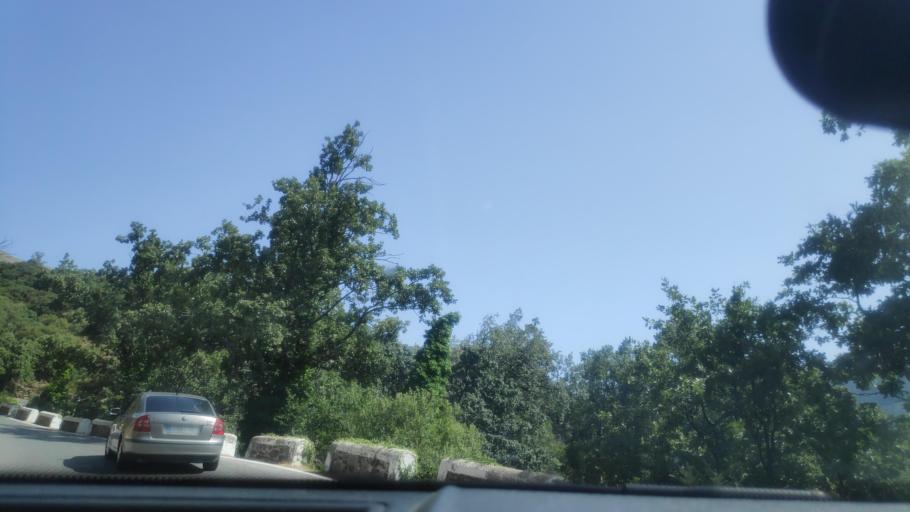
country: ES
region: Andalusia
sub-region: Provincia de Granada
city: Busquistar
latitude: 36.9483
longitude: -3.2853
